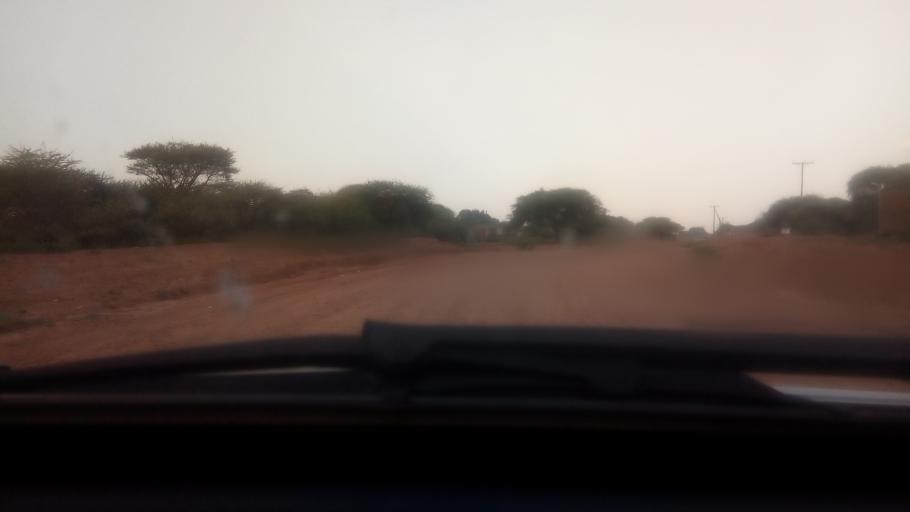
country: BW
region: Kgatleng
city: Bokaa
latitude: -24.4311
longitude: 26.0068
